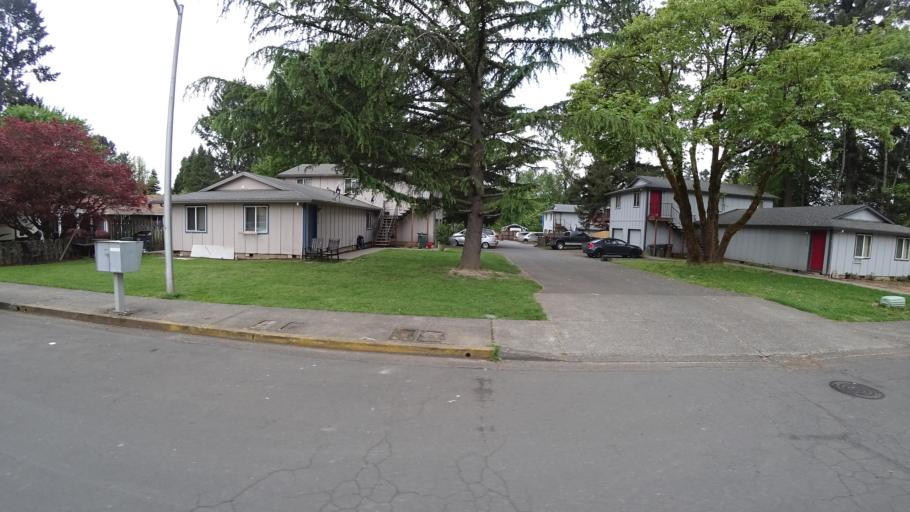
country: US
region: Oregon
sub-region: Washington County
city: Hillsboro
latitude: 45.5421
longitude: -123.0001
